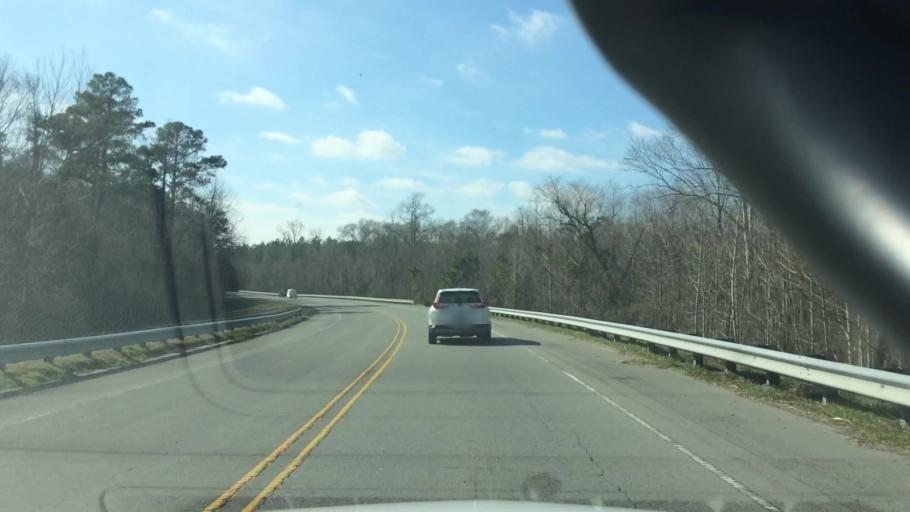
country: US
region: North Carolina
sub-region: Duplin County
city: Beulaville
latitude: 34.8304
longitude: -77.8330
